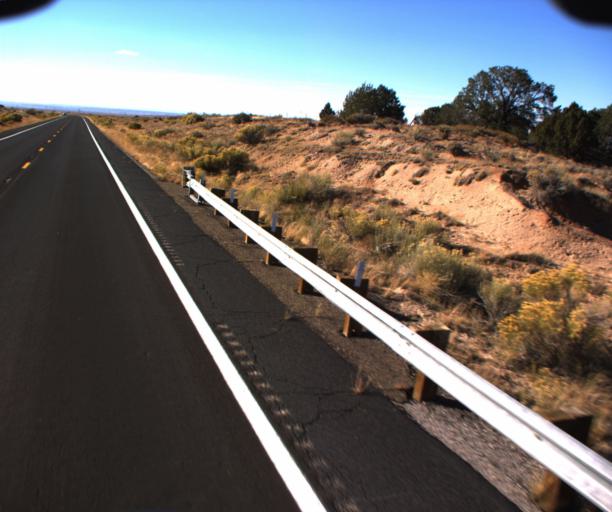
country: US
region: Arizona
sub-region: Coconino County
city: Kaibito
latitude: 36.6149
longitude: -110.9313
